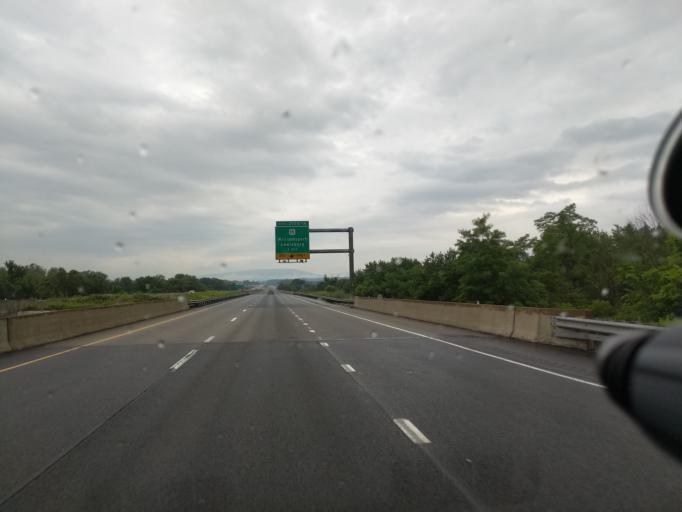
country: US
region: Pennsylvania
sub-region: Union County
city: New Columbia
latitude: 41.0517
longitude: -76.8491
